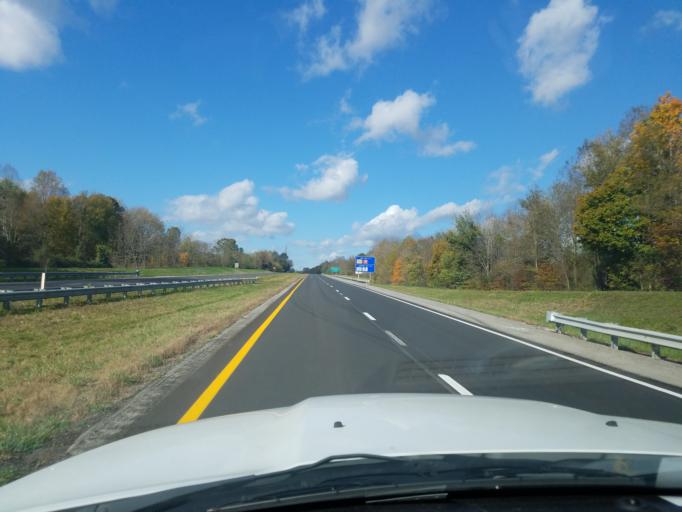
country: US
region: Kentucky
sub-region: Adair County
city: Columbia
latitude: 37.0899
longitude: -85.2835
